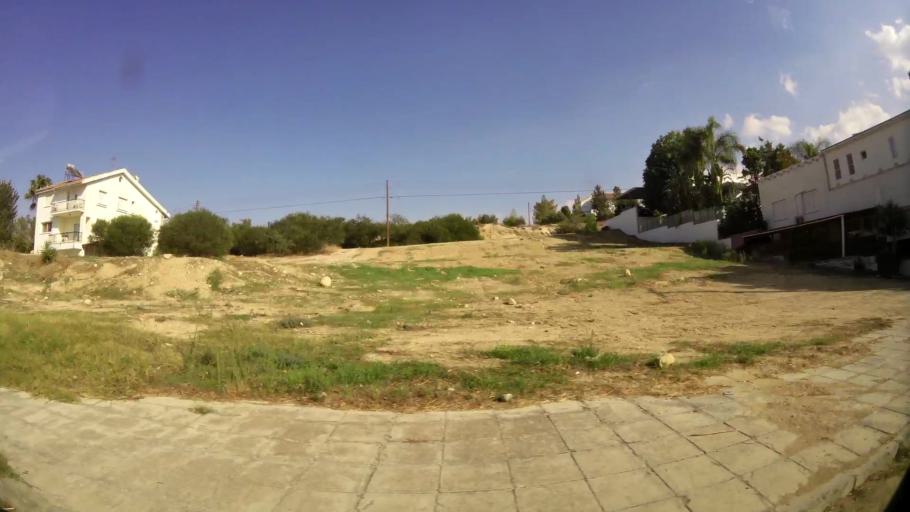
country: CY
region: Lefkosia
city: Kato Deftera
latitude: 35.1482
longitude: 33.3006
